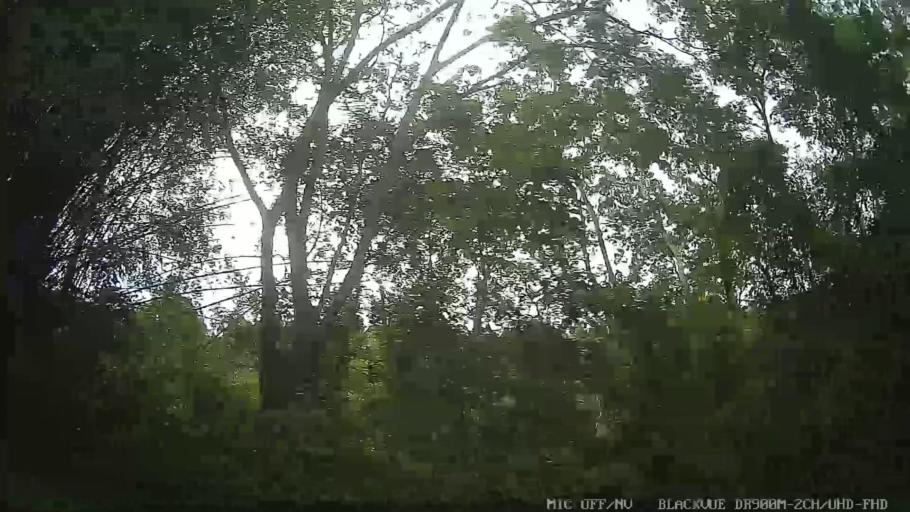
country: BR
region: Sao Paulo
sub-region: Santa Branca
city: Santa Branca
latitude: -23.5289
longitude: -45.7157
